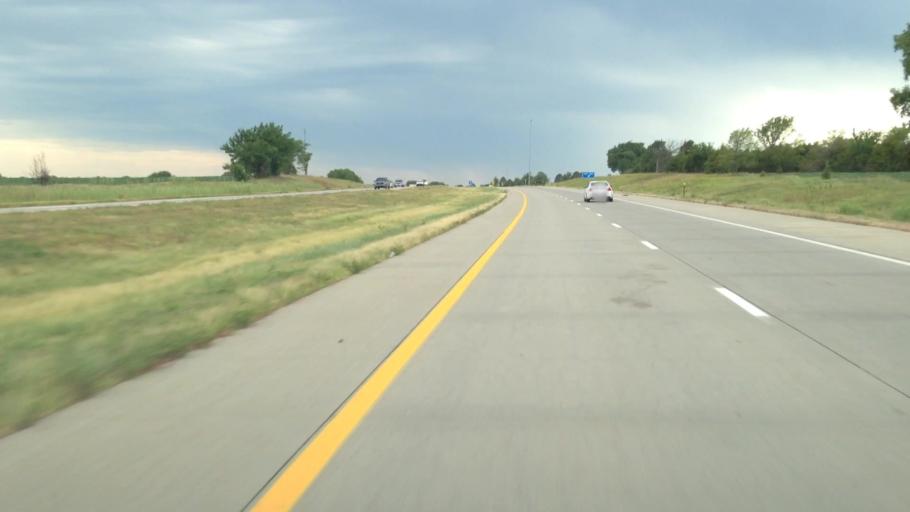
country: US
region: Kansas
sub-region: Franklin County
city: Ottawa
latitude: 38.5290
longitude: -95.3975
